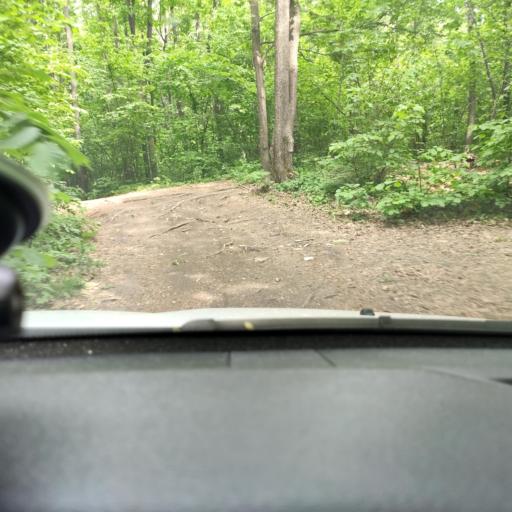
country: RU
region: Samara
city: Volzhskiy
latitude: 53.3245
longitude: 50.1981
